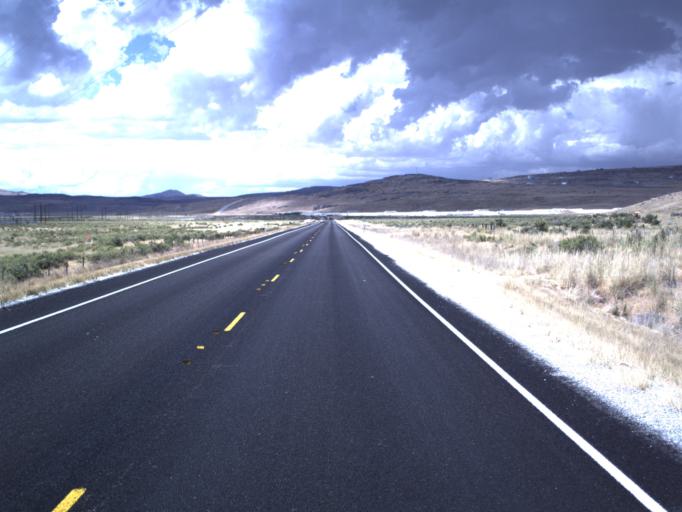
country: US
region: Utah
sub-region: Box Elder County
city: Tremonton
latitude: 41.6171
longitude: -112.3812
